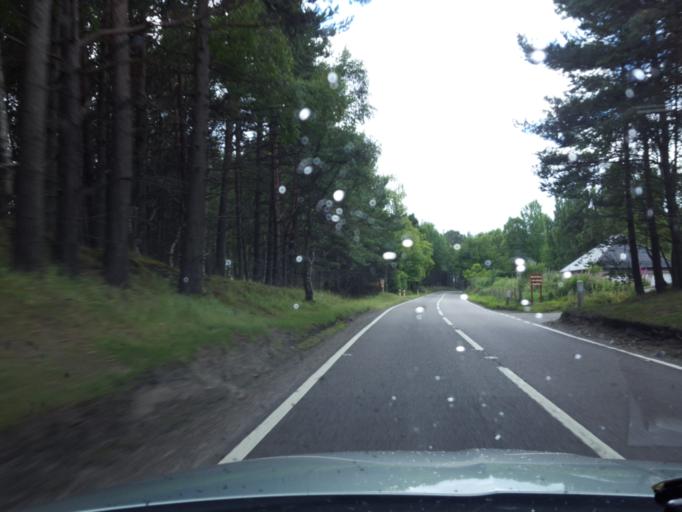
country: GB
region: Scotland
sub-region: Highland
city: Aviemore
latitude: 57.2430
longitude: -3.8042
